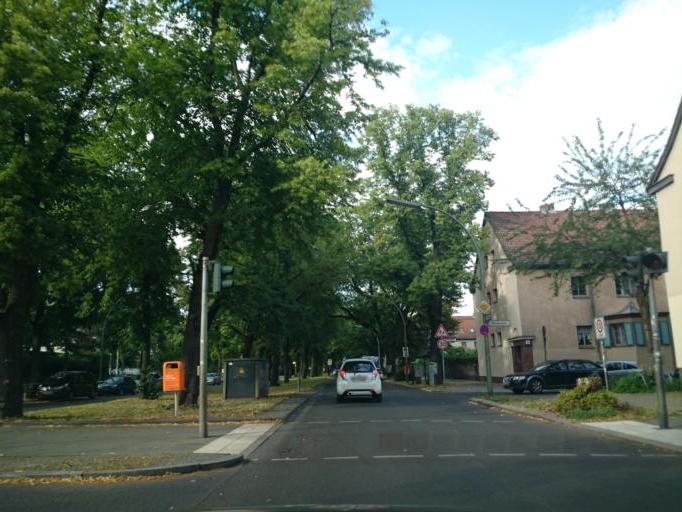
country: DE
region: Berlin
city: Plaenterwald
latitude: 52.4713
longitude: 13.4669
